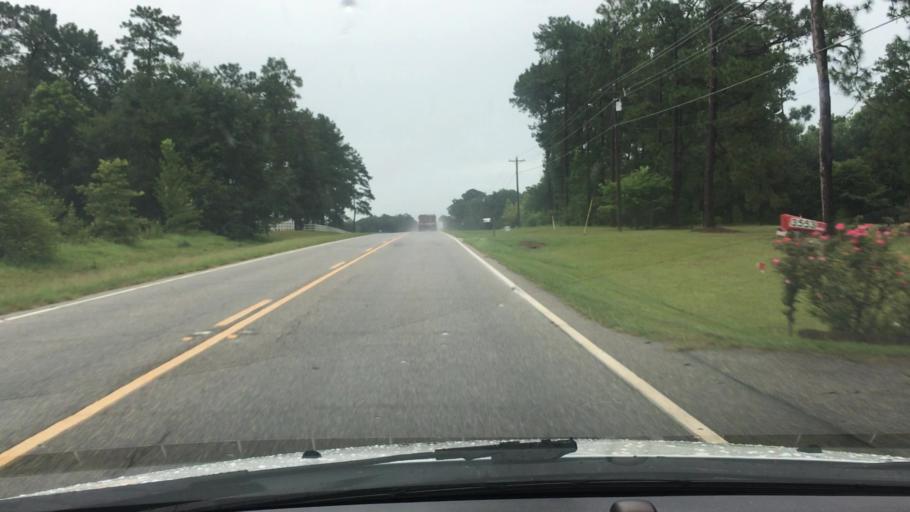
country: US
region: Georgia
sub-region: Grady County
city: Cairo
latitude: 30.7971
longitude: -84.2611
